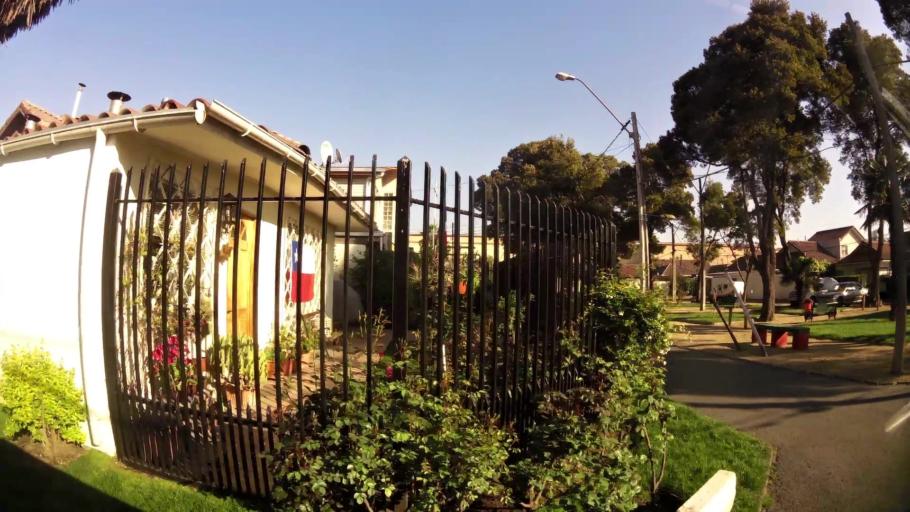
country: CL
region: Santiago Metropolitan
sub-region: Provincia de Santiago
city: Lo Prado
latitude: -33.4851
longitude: -70.7495
